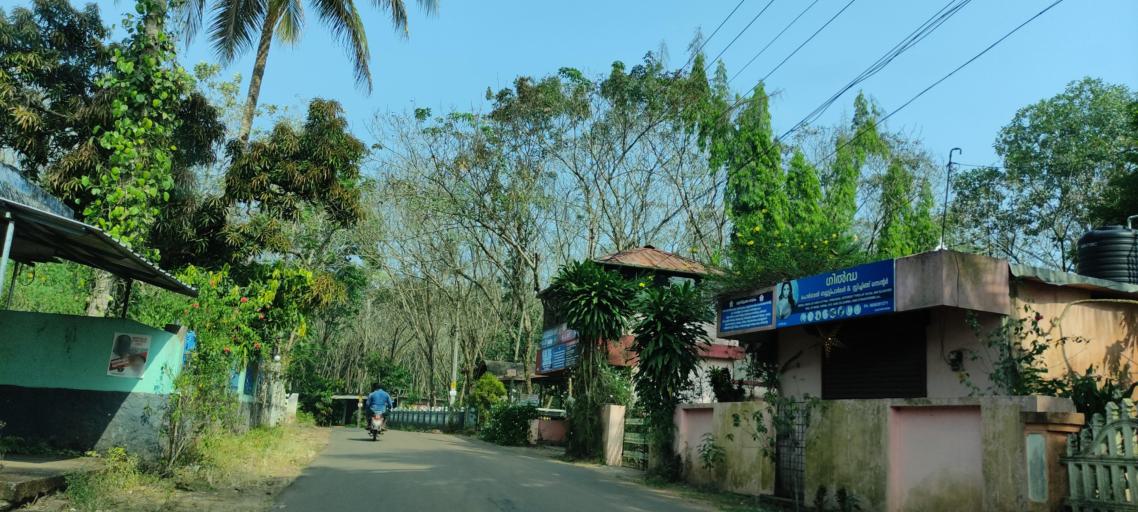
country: IN
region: Kerala
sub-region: Ernakulam
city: Piravam
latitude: 9.8188
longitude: 76.5182
